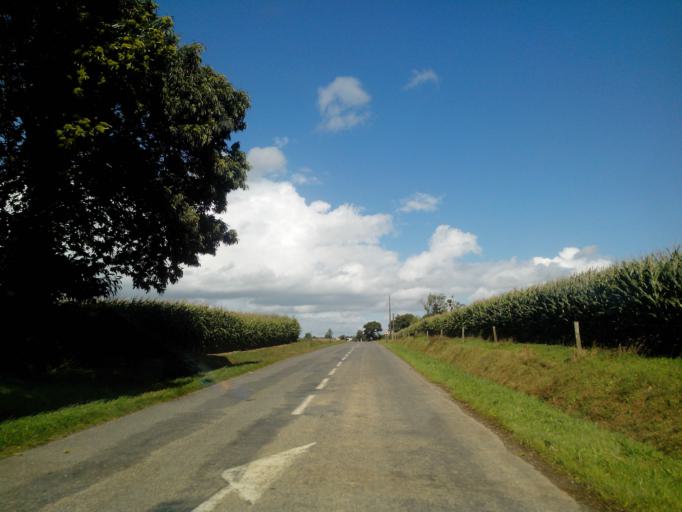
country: FR
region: Brittany
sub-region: Departement des Cotes-d'Armor
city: Merdrignac
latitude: 48.1786
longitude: -2.4144
